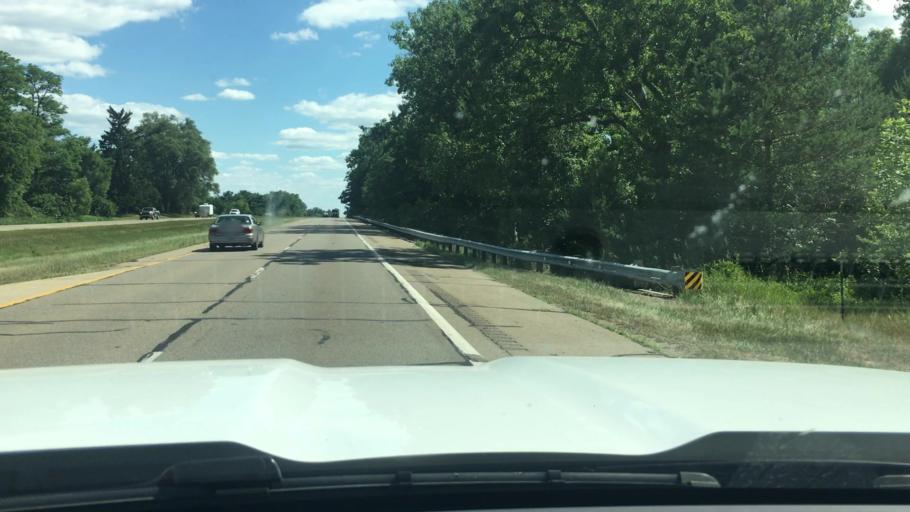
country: US
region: Michigan
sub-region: Clinton County
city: Saint Johns
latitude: 43.1118
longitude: -84.5635
